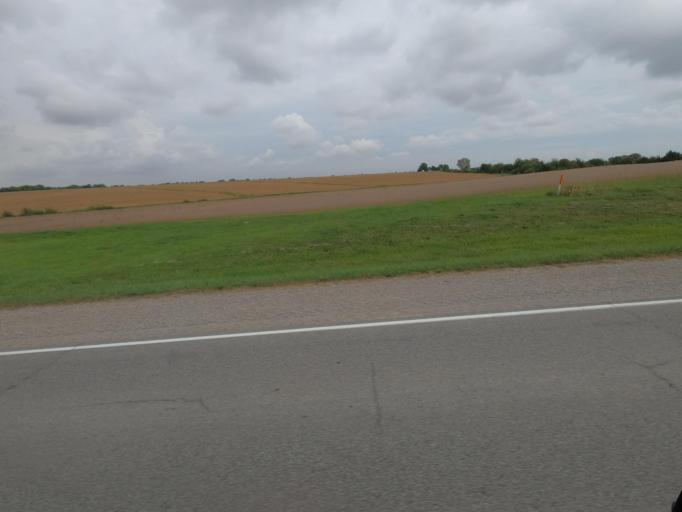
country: US
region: Iowa
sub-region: Wapello County
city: Ottumwa
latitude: 40.9628
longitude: -92.2364
